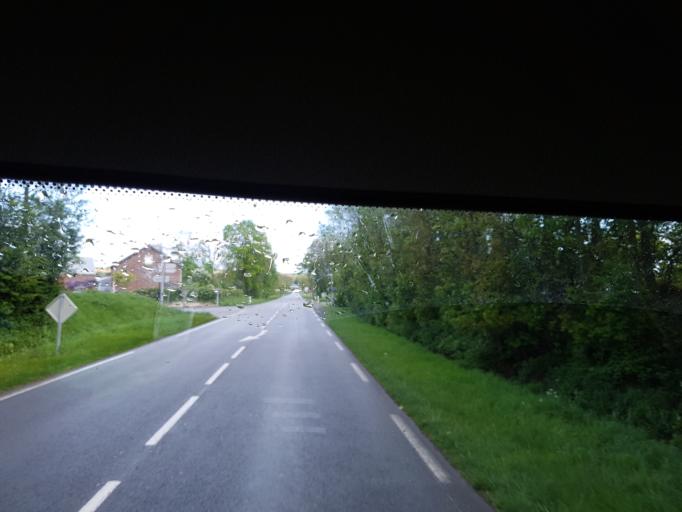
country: FR
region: Picardie
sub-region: Departement de l'Aisne
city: Holnon
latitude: 49.9267
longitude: 3.2497
